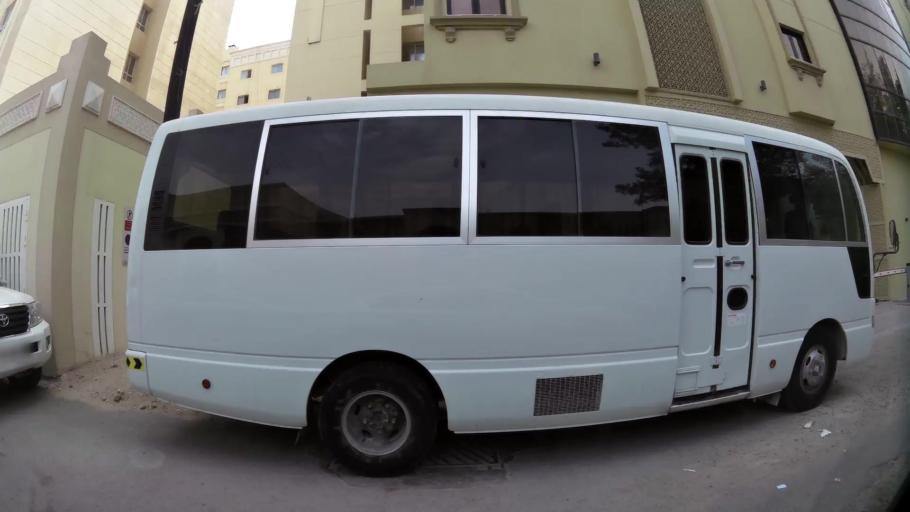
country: QA
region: Baladiyat ad Dawhah
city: Doha
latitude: 25.2872
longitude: 51.4977
